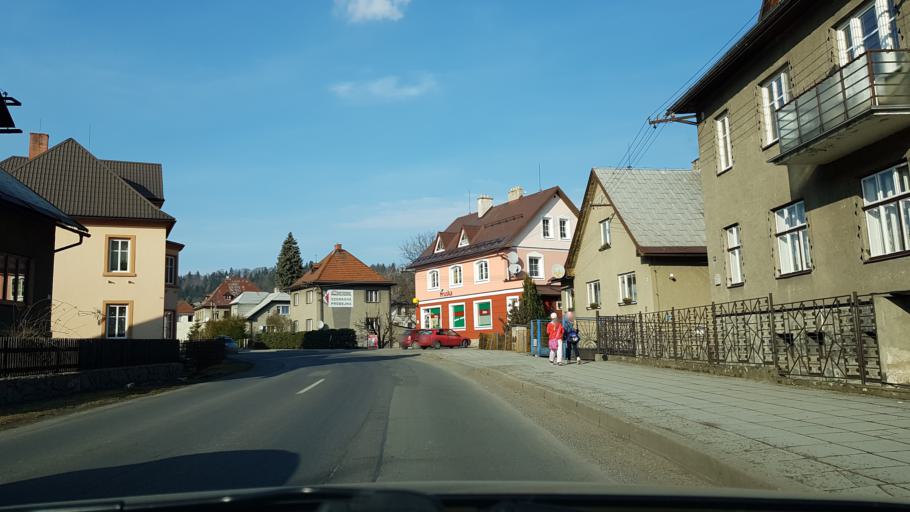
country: CZ
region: Olomoucky
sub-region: Okres Sumperk
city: Hanusovice
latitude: 50.0720
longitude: 16.9319
